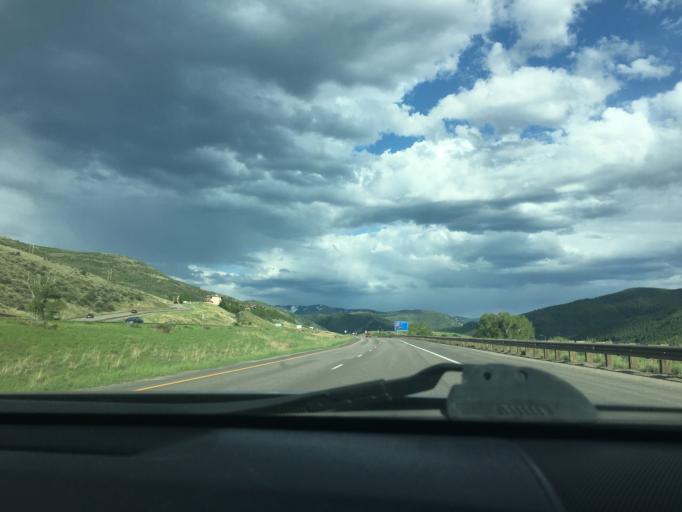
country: US
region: Colorado
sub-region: Eagle County
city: Avon
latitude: 39.6342
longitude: -106.5157
